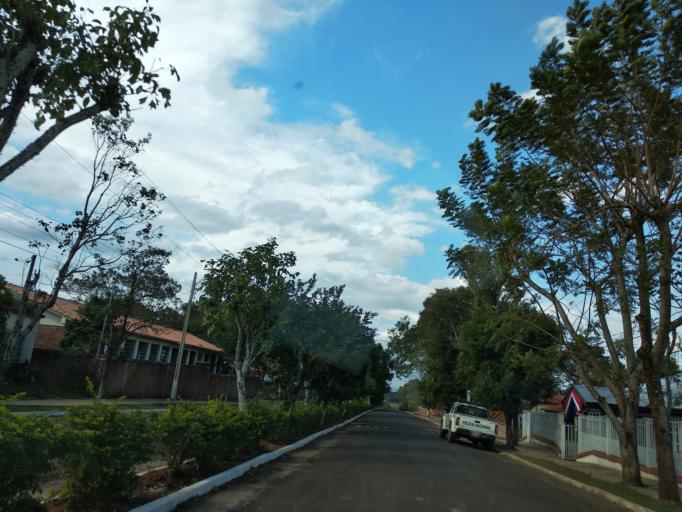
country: PY
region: Itapua
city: San Juan del Parana
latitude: -27.3030
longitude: -55.9653
